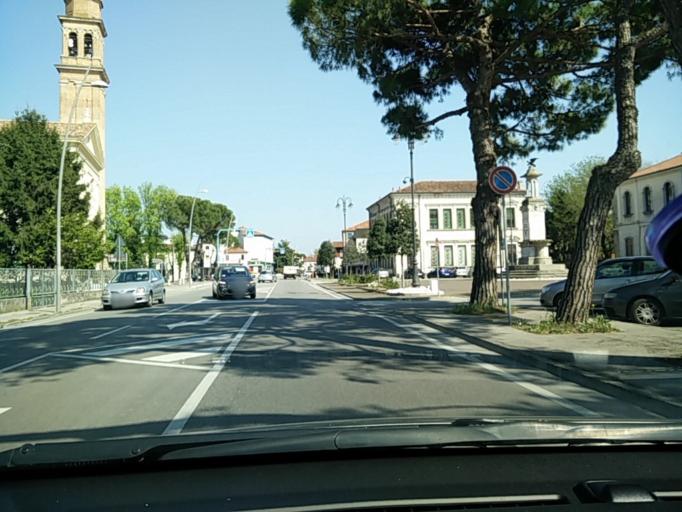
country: IT
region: Veneto
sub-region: Provincia di Venezia
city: Fiesso
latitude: 45.4169
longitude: 12.0301
